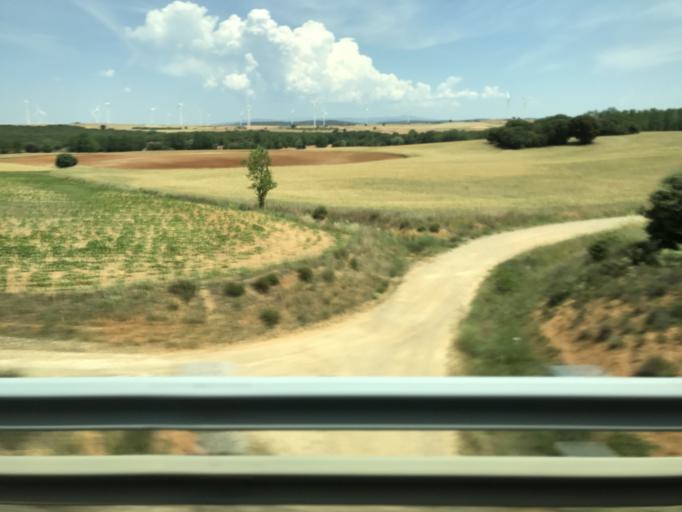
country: ES
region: Castille and Leon
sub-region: Provincia de Burgos
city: Valdorros
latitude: 42.1651
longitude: -3.7018
